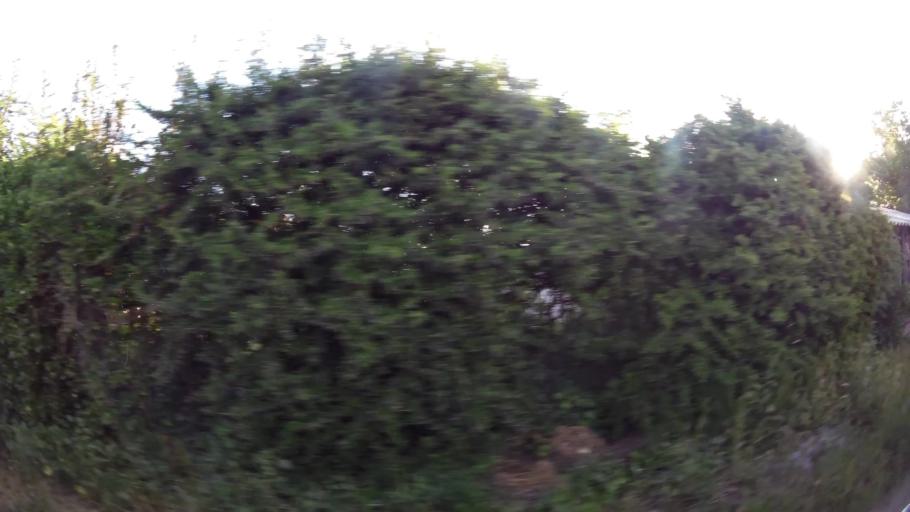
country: CL
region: Santiago Metropolitan
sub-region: Provincia de Talagante
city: Penaflor
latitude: -33.5984
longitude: -70.8485
